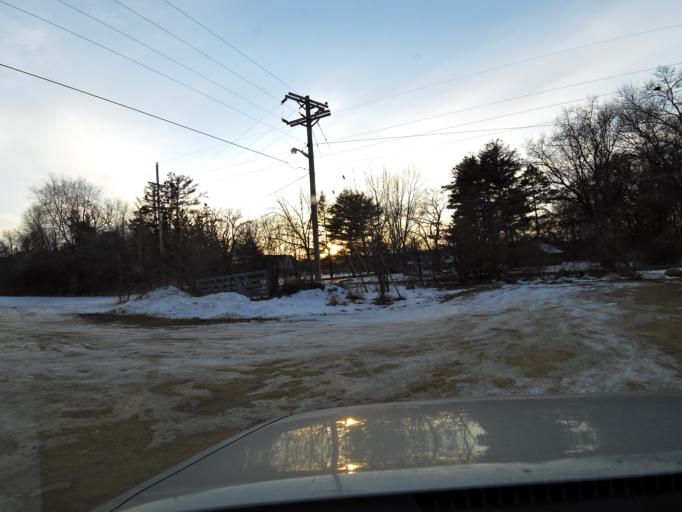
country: US
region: Wisconsin
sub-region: Saint Croix County
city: North Hudson
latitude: 44.9974
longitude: -92.7615
